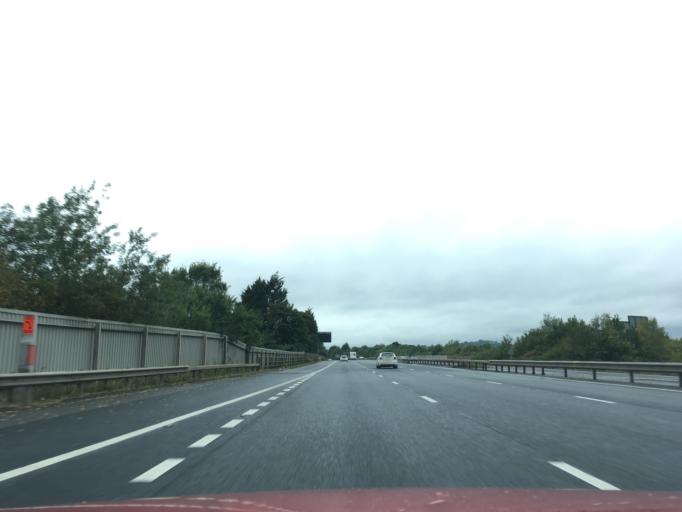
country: GB
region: England
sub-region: Gloucestershire
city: Churchdown
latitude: 51.8563
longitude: -2.1755
